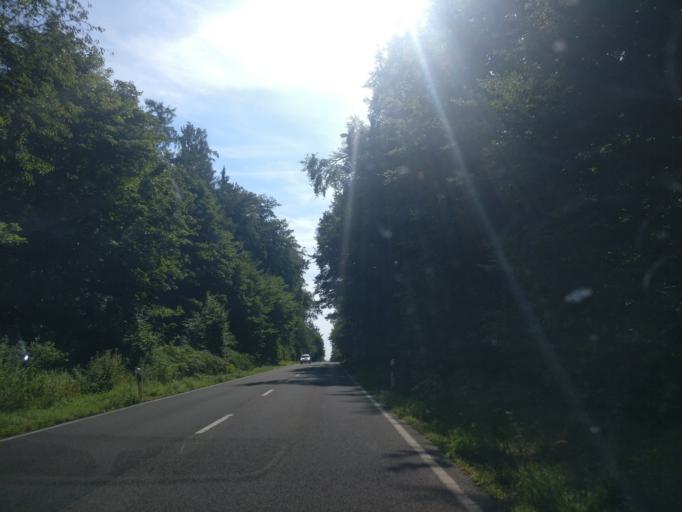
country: LU
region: Luxembourg
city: Bereldange
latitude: 49.6415
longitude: 6.1045
